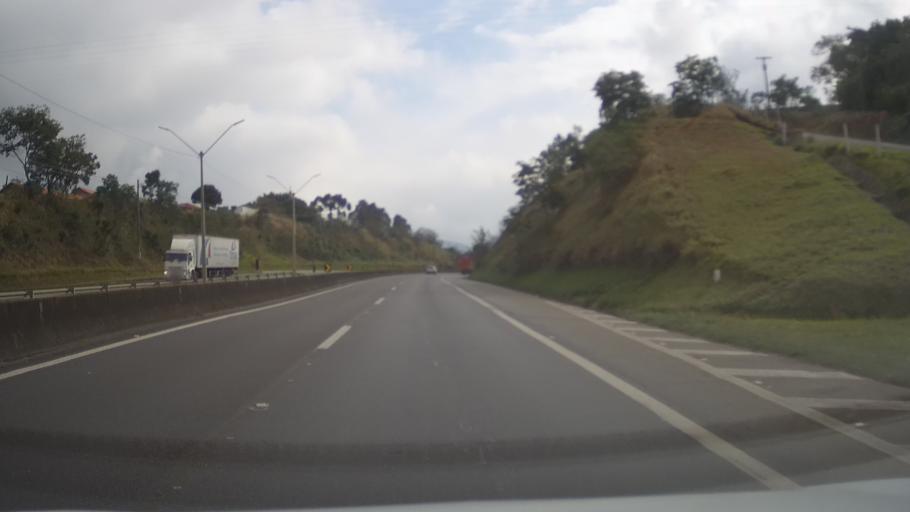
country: BR
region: Minas Gerais
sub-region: Extrema
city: Extrema
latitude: -22.8970
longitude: -46.4183
